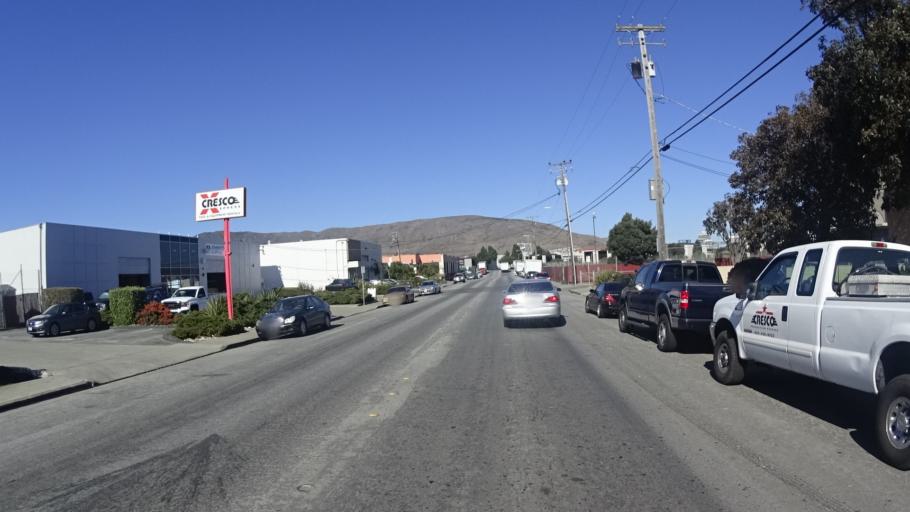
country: US
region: California
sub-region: San Mateo County
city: South San Francisco
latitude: 37.6470
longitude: -122.4096
